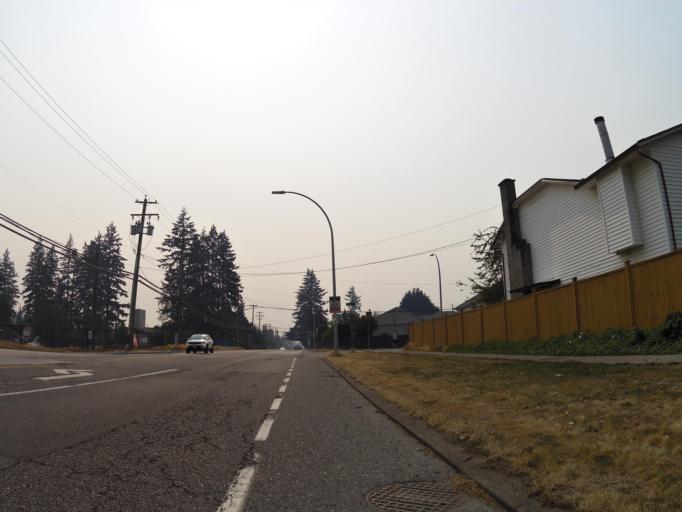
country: CA
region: British Columbia
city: Surrey
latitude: 49.1368
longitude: -122.8567
